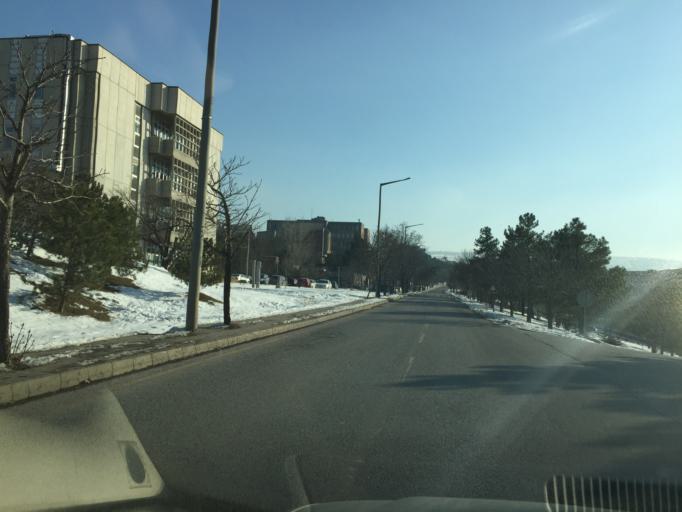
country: TR
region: Ankara
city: Ankara
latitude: 39.8971
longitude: 32.7805
